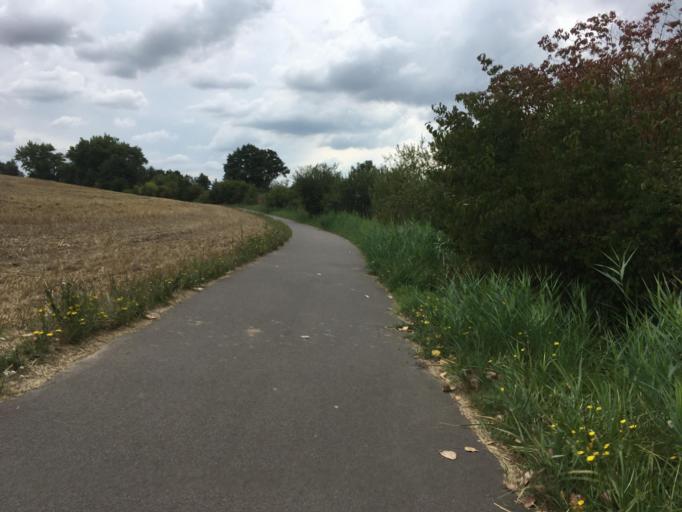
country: DE
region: Brandenburg
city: Prenzlau
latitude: 53.2874
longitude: 13.8785
